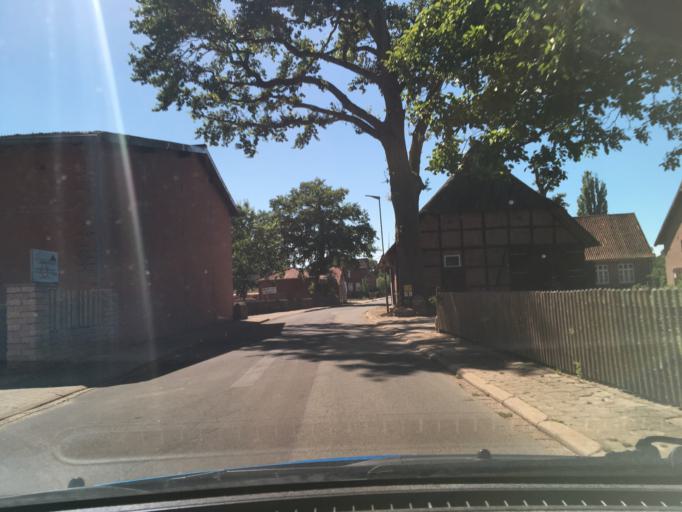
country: DE
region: Lower Saxony
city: Winsen
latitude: 53.3416
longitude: 10.1954
